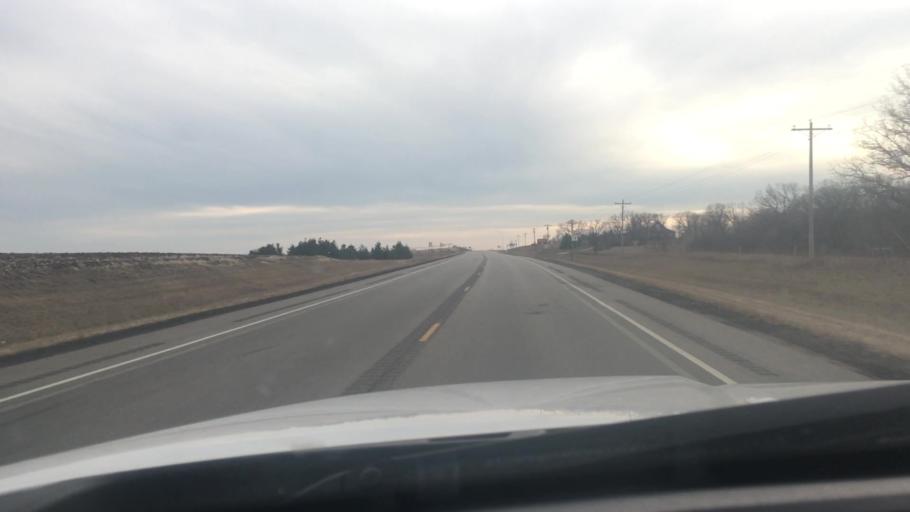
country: US
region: Minnesota
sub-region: Otter Tail County
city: Perham
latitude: 46.3147
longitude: -95.7185
